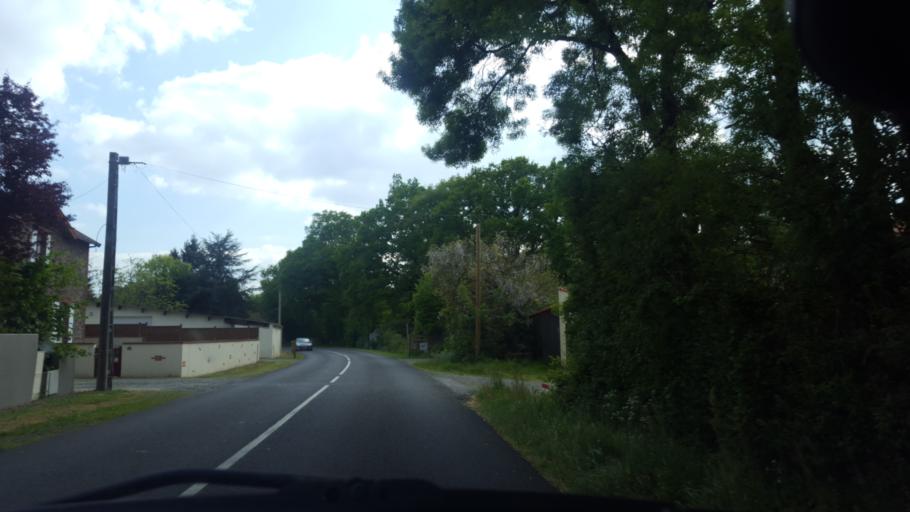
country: FR
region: Pays de la Loire
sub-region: Departement de la Loire-Atlantique
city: La Limouziniere
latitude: 47.0024
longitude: -1.5880
